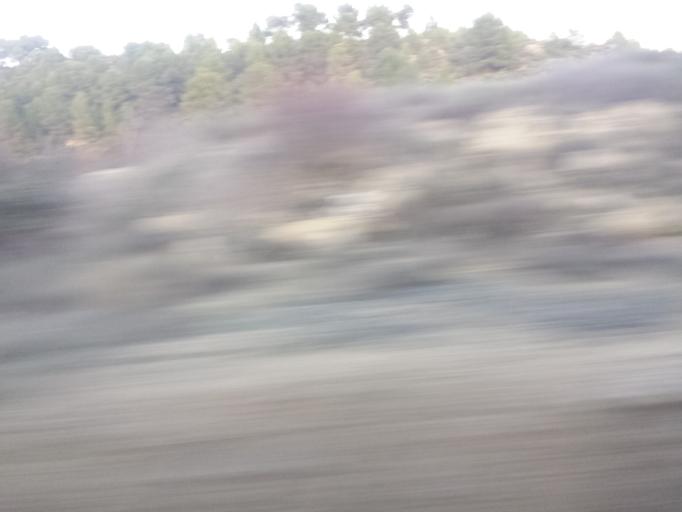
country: ES
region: Aragon
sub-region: Provincia de Zaragoza
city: Santa Eulalia de Gallego
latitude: 42.3078
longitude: -0.7206
